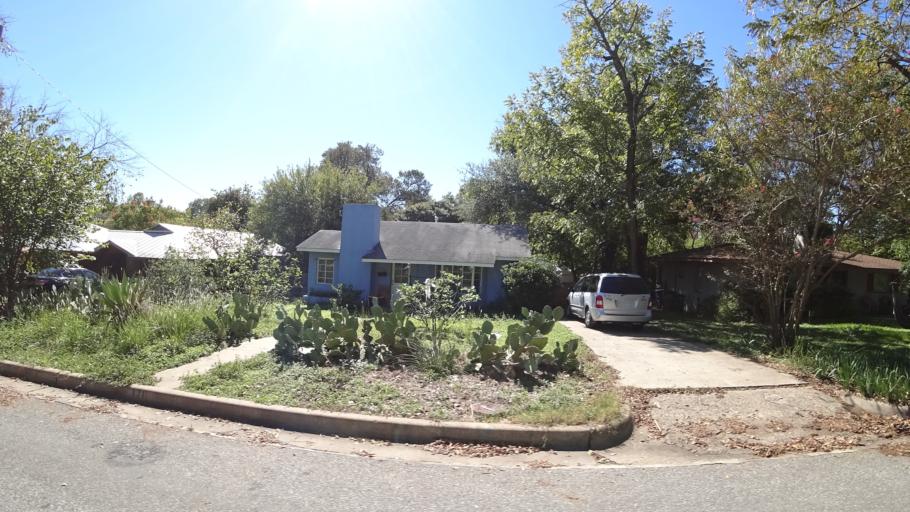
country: US
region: Texas
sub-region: Travis County
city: Austin
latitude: 30.2899
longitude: -97.7134
